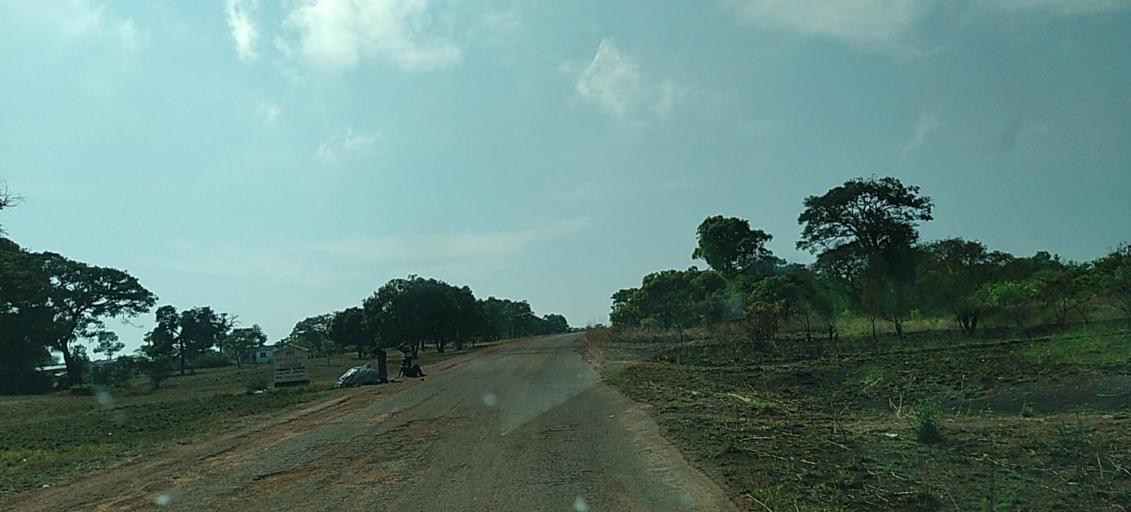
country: ZM
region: North-Western
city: Mwinilunga
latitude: -11.7720
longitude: 25.0125
